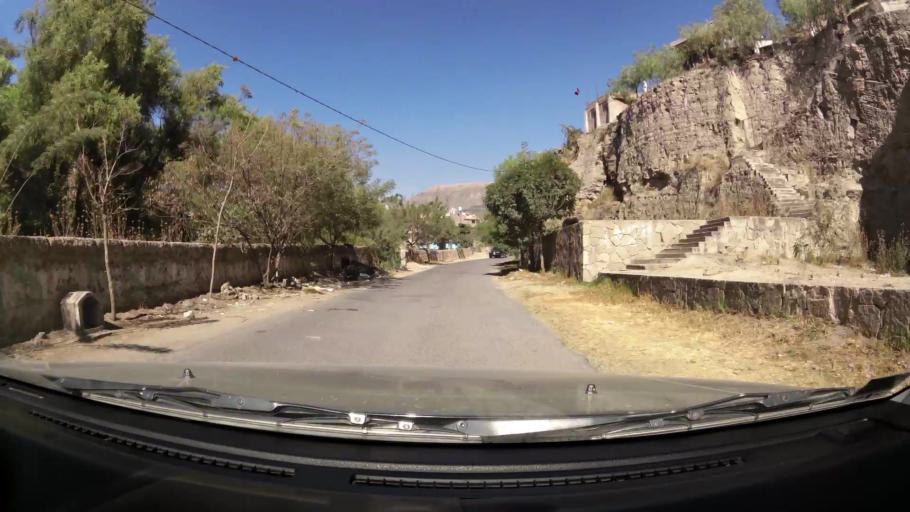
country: PE
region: Ayacucho
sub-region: Provincia de Huamanga
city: Ayacucho
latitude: -13.1623
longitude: -74.2191
